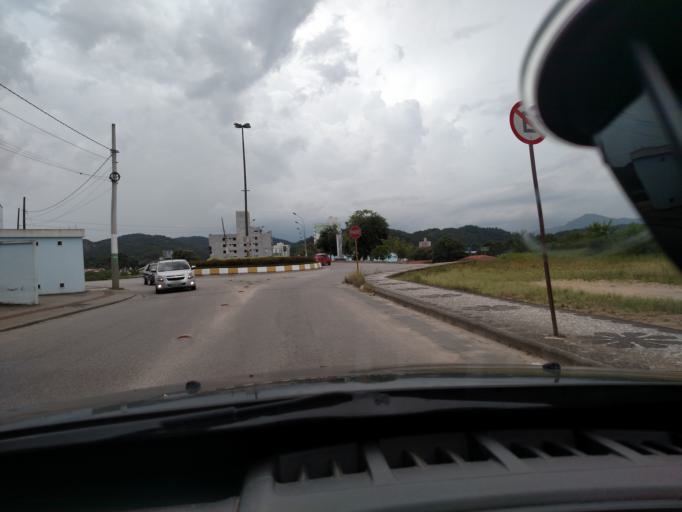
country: BR
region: Santa Catarina
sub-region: Brusque
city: Brusque
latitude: -27.0825
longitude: -48.9069
